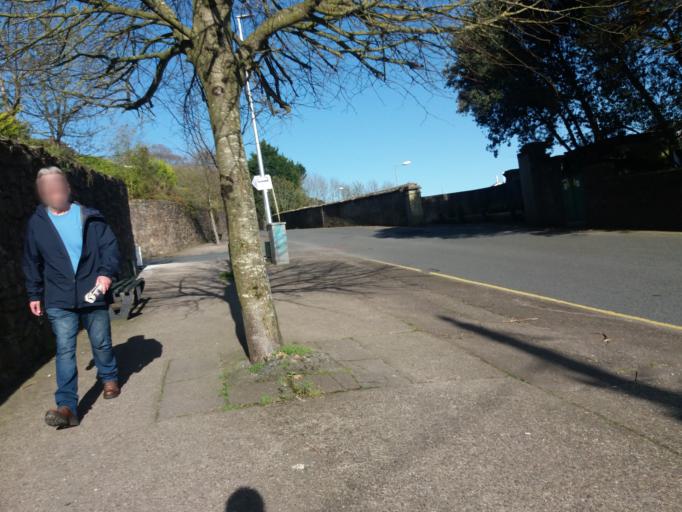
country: IE
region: Munster
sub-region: County Cork
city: Cork
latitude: 51.9049
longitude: -8.4521
